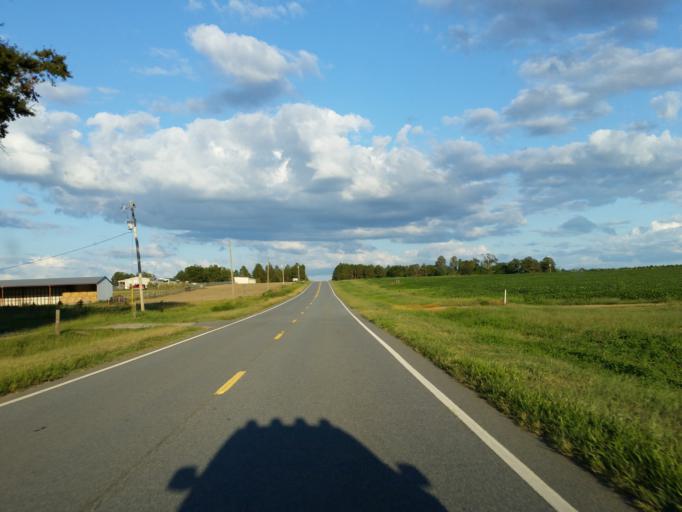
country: US
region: Georgia
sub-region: Dooly County
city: Vienna
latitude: 32.0862
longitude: -83.7334
